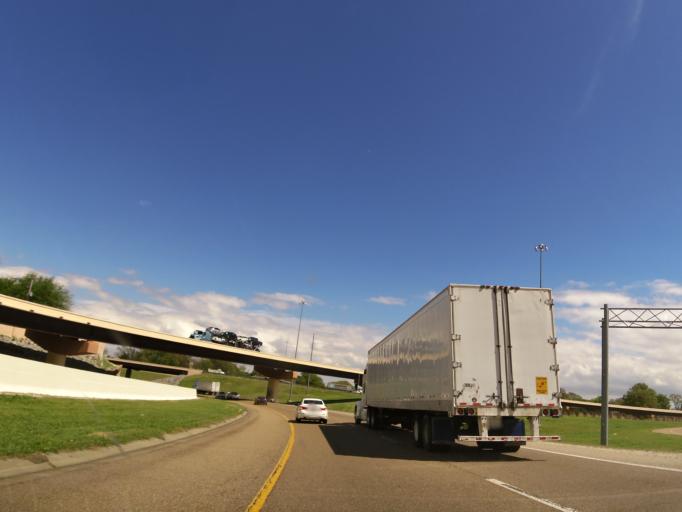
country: US
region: Tennessee
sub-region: Shelby County
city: Memphis
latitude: 35.1497
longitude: -90.0250
